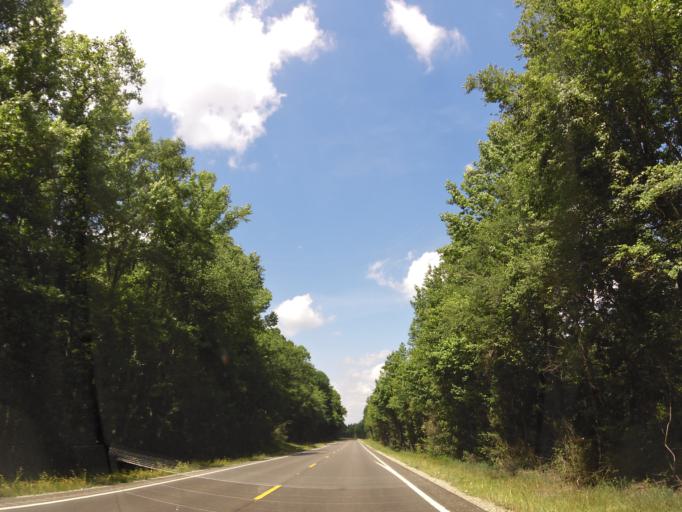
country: US
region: Alabama
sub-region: Marion County
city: Guin
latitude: 33.9524
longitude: -87.9727
